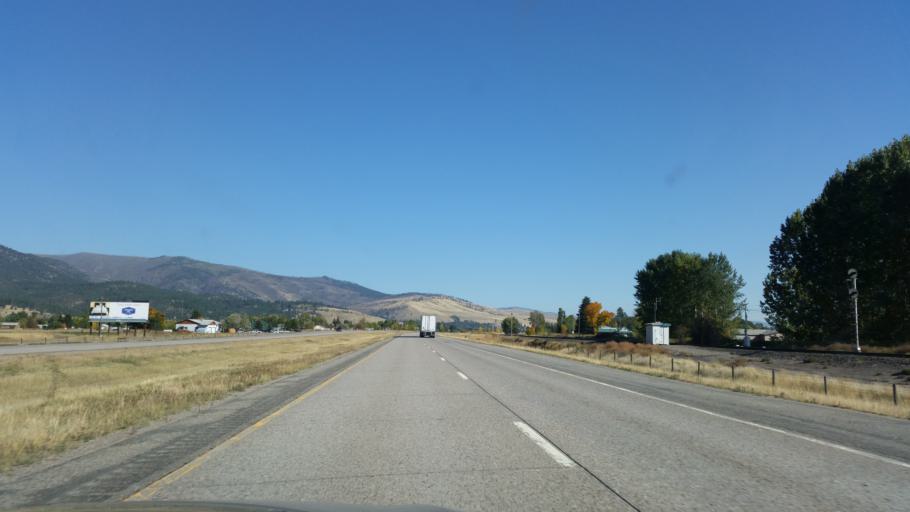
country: US
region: Montana
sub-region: Missoula County
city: Frenchtown
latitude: 47.0261
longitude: -114.2798
